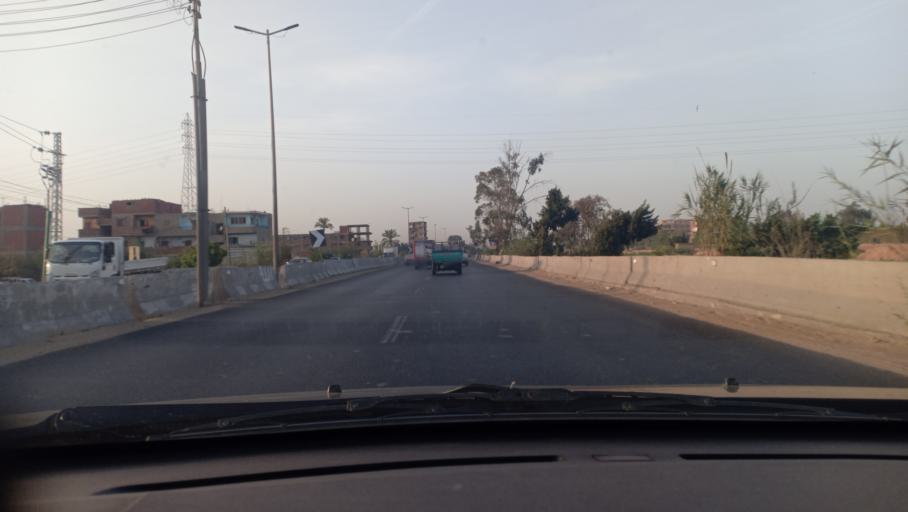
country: EG
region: Muhafazat al Minufiyah
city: Quwaysina
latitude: 30.5580
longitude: 31.2683
